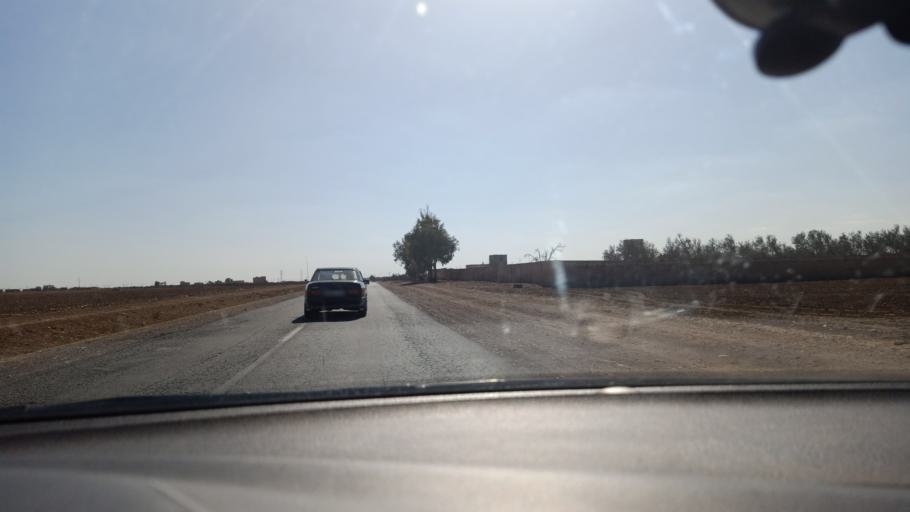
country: MA
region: Doukkala-Abda
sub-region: Safi
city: Youssoufia
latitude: 32.1233
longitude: -8.6028
